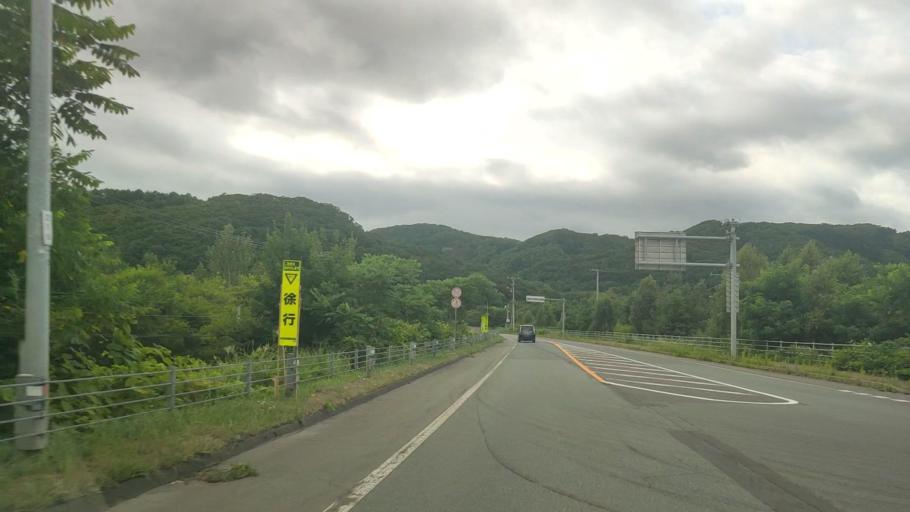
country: JP
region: Hokkaido
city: Niseko Town
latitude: 42.5892
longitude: 140.7052
